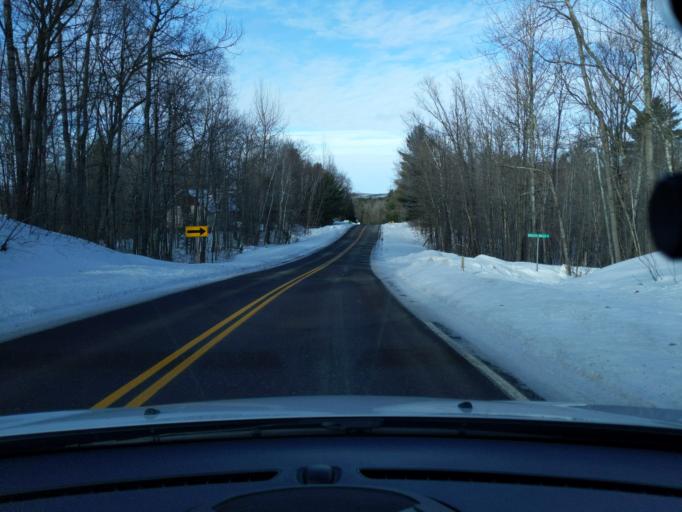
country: US
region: Wisconsin
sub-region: Sawyer County
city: Little Round Lake
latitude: 46.1180
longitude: -91.3406
